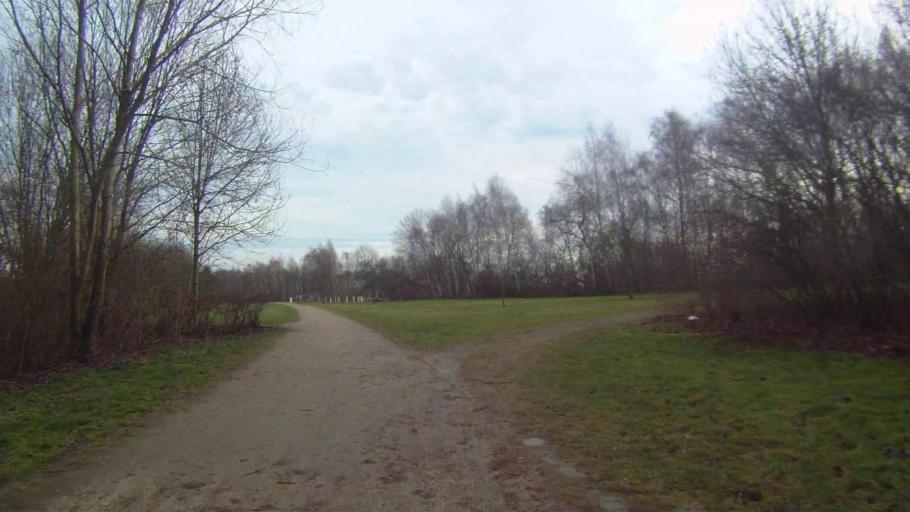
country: DE
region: Berlin
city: Lichtenrade
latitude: 52.4106
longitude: 13.4197
